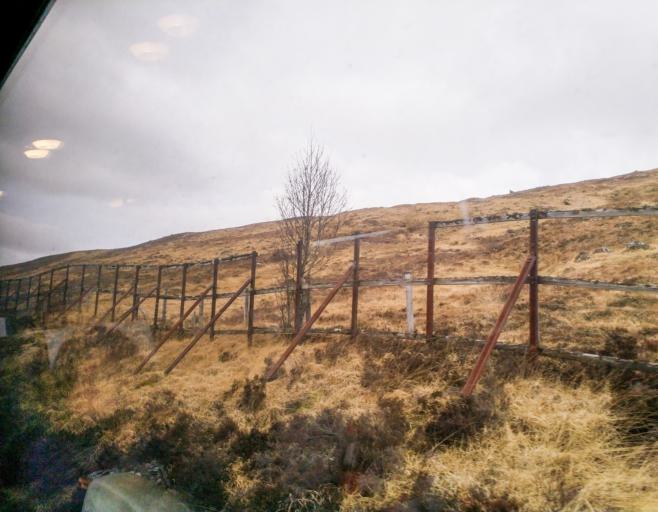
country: GB
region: Scotland
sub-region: Highland
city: Spean Bridge
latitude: 56.7754
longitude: -4.7181
